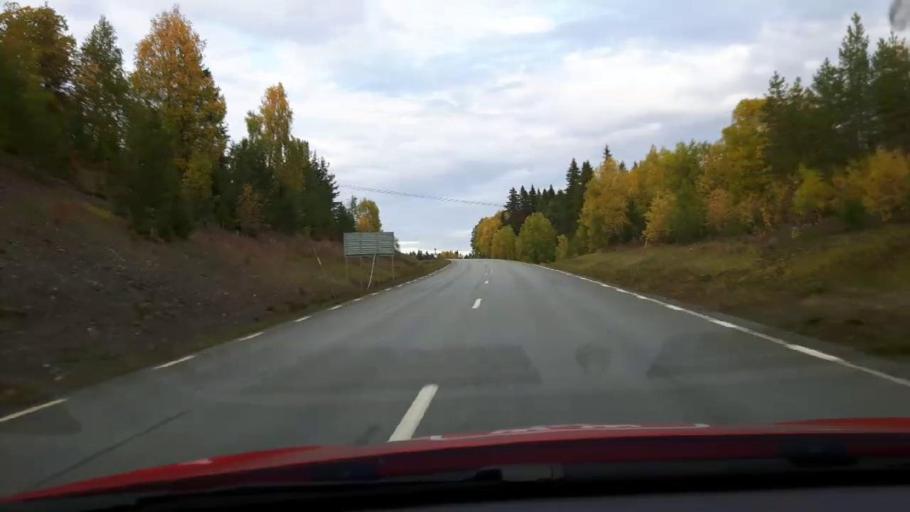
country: SE
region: Jaemtland
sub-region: Krokoms Kommun
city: Krokom
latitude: 63.3600
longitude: 14.4999
